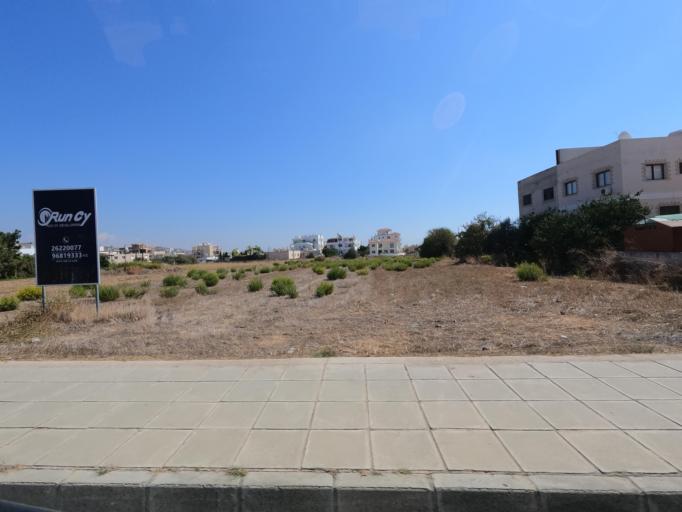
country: CY
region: Pafos
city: Paphos
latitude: 34.7664
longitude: 32.4470
